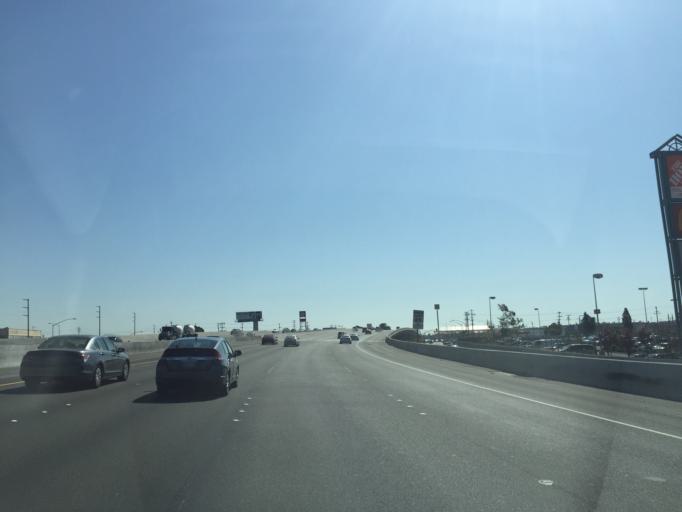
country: US
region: California
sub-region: Alameda County
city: Alameda
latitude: 37.7709
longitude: -122.2229
